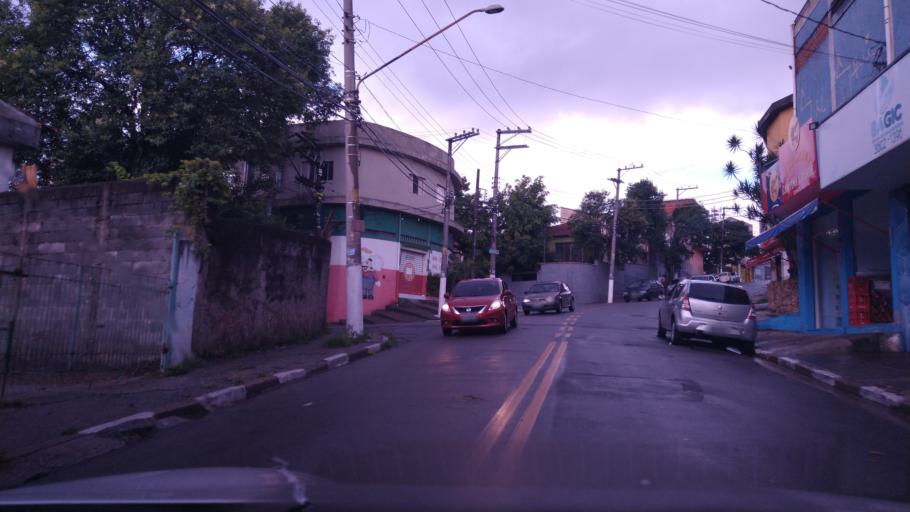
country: BR
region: Sao Paulo
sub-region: Osasco
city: Osasco
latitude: -23.5143
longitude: -46.7810
